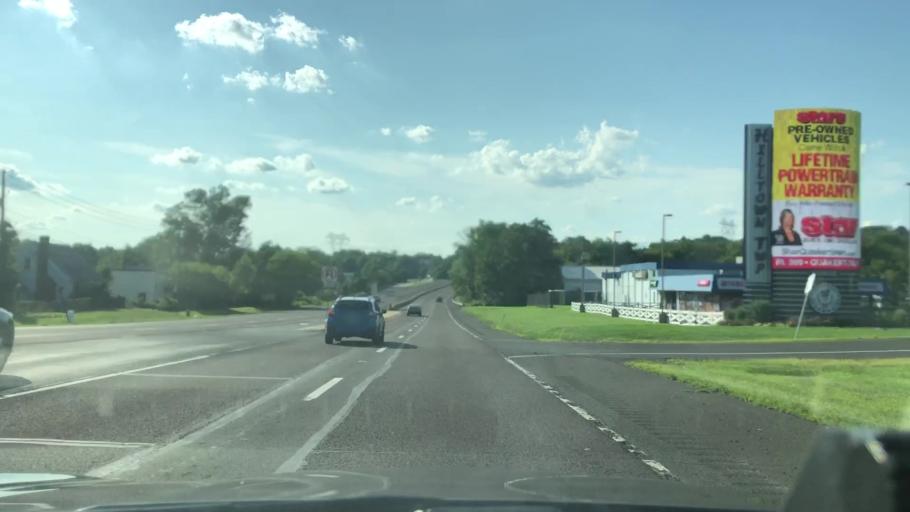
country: US
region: Pennsylvania
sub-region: Montgomery County
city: Hatfield
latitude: 40.3027
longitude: -75.2910
